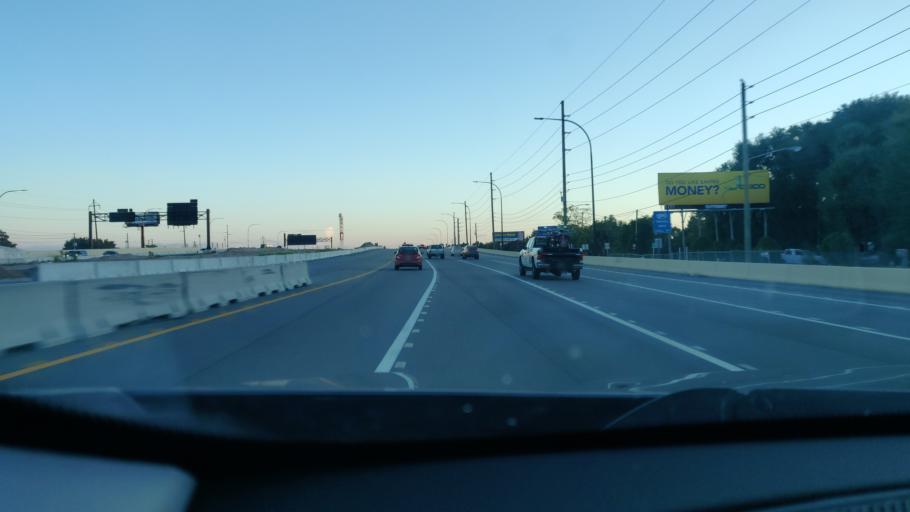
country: US
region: Florida
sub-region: Orange County
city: Eatonville
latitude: 28.6217
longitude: -81.3869
